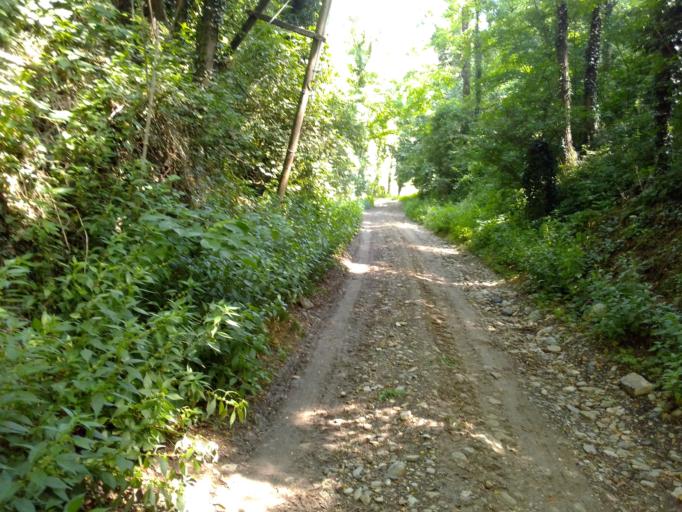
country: IT
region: Emilia-Romagna
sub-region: Provincia di Piacenza
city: Borgonovo Valtidone
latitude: 44.9827
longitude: 9.4737
